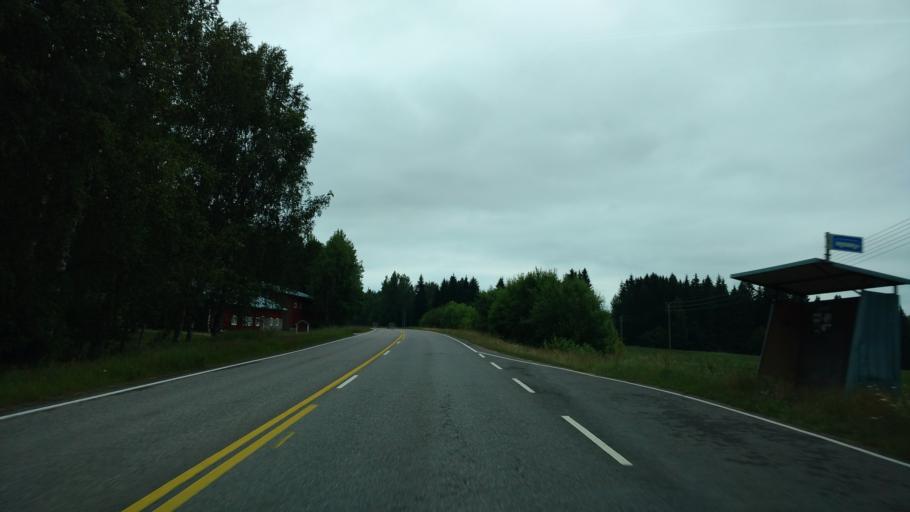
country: FI
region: Varsinais-Suomi
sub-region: Salo
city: Kiikala
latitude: 60.4108
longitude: 23.5856
